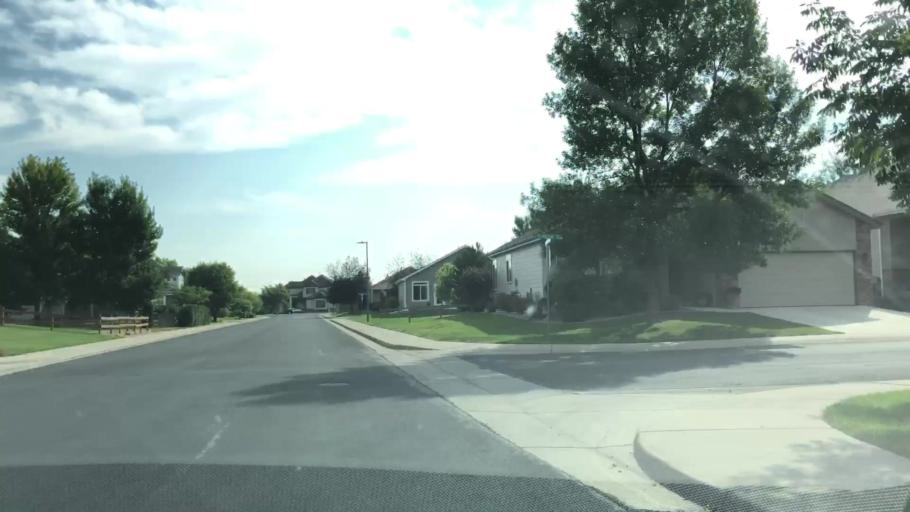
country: US
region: Colorado
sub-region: Larimer County
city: Loveland
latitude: 40.4305
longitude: -105.0536
